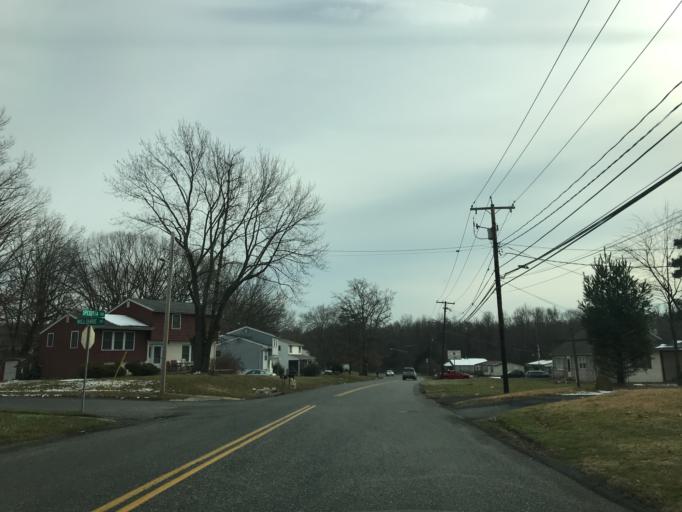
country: US
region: Maryland
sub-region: Harford County
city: Perryman
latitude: 39.4792
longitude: -76.2070
